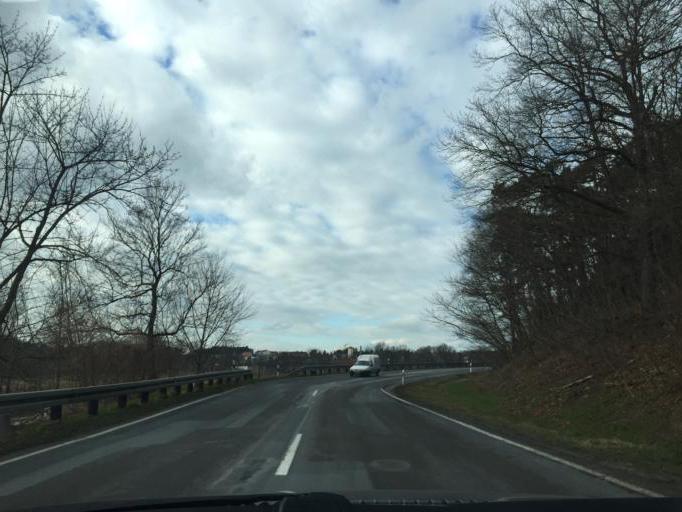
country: DE
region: Saxony
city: Ottendorf-Okrilla
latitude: 51.1815
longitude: 13.7998
